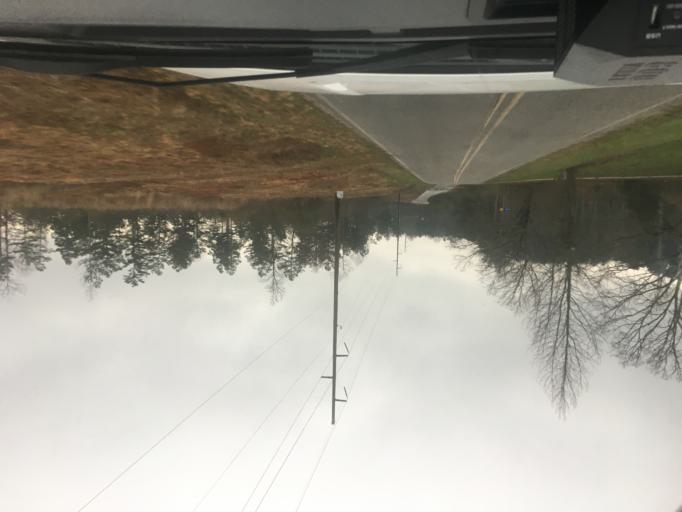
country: US
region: Georgia
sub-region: Dawson County
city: Dawsonville
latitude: 34.4402
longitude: -84.2243
